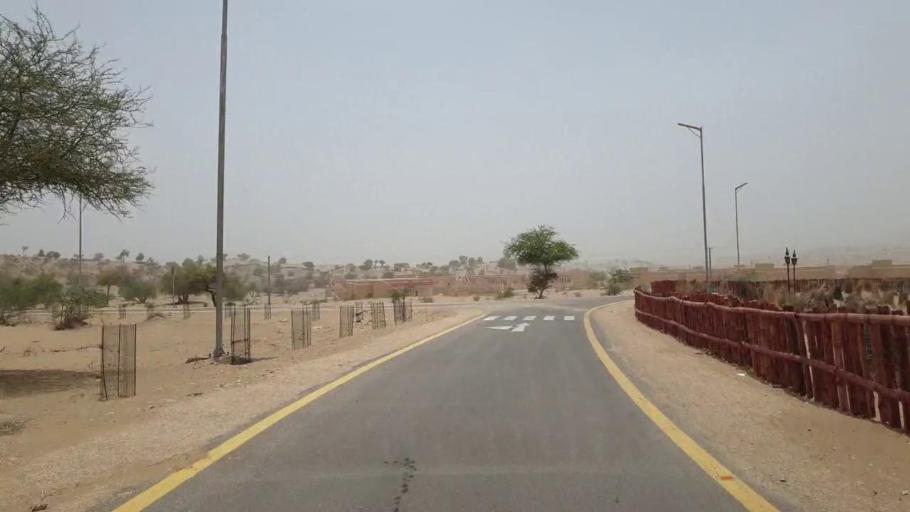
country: PK
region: Sindh
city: Islamkot
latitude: 24.7241
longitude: 70.3241
